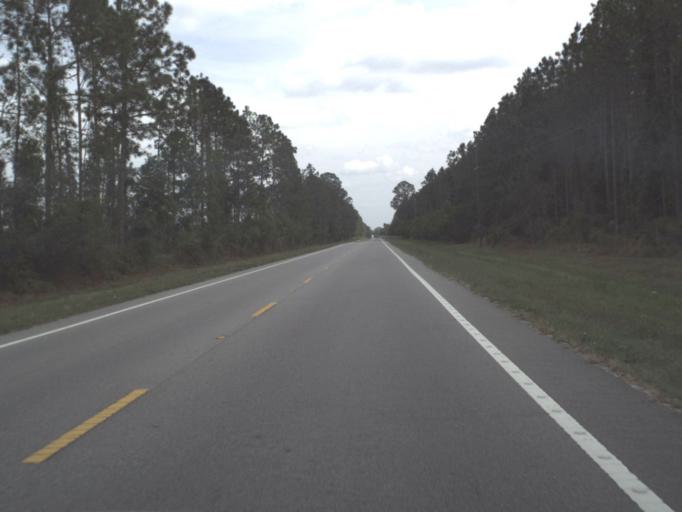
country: US
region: Florida
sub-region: Putnam County
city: Crescent City
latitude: 29.5326
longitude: -81.5166
